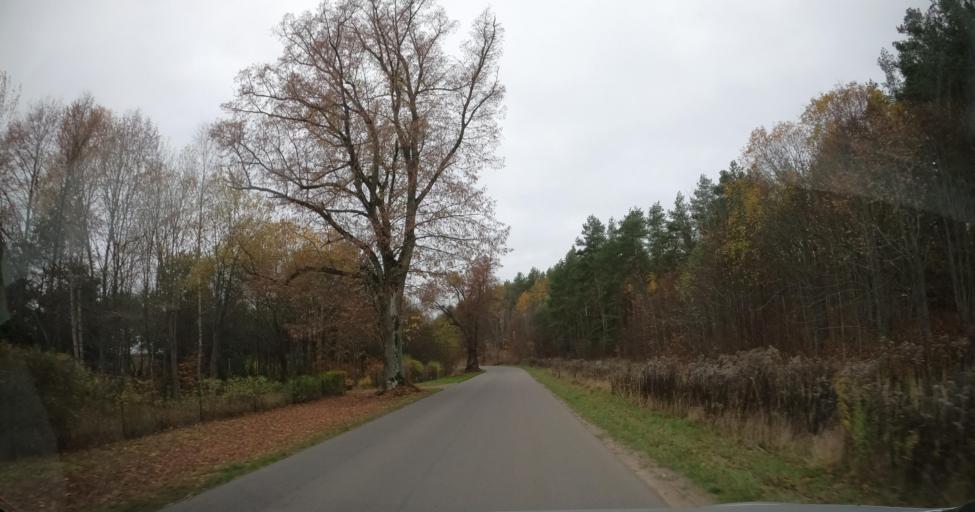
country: PL
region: West Pomeranian Voivodeship
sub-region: Powiat swidwinski
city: Polczyn-Zdroj
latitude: 53.7826
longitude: 16.1749
